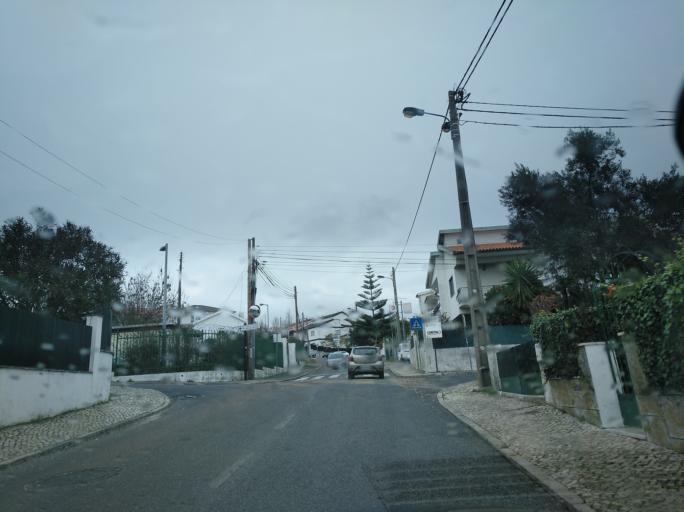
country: PT
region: Lisbon
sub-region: Odivelas
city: Famoes
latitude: 38.7929
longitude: -9.2110
